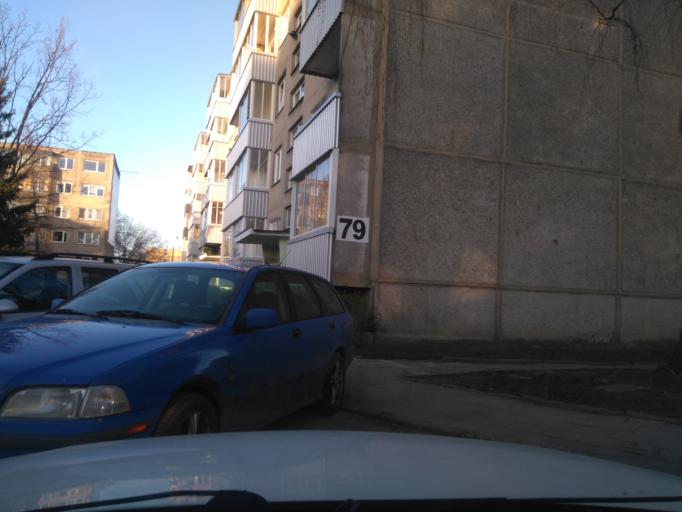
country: LT
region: Kauno apskritis
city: Dainava (Kaunas)
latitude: 54.9228
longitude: 23.9770
